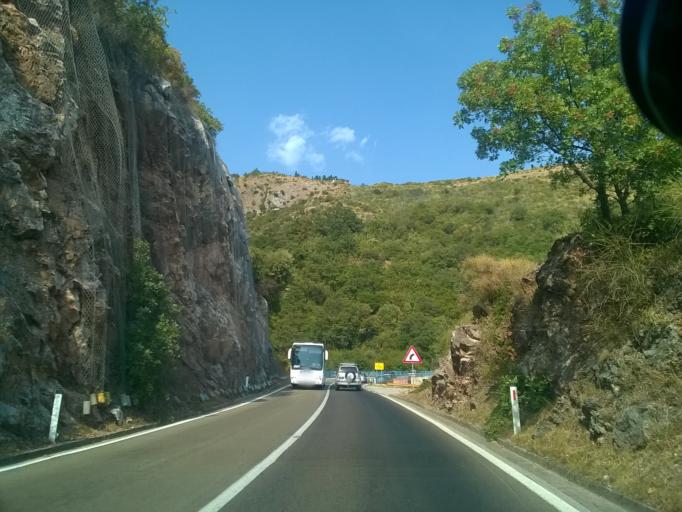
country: ME
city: Petrovac na Moru
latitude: 42.2113
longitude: 18.9420
